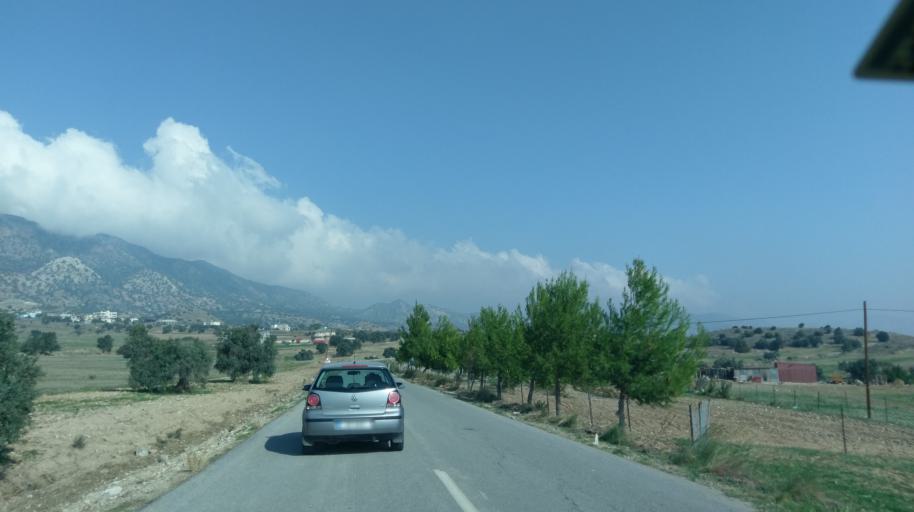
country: CY
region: Ammochostos
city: Lefkonoiko
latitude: 35.2895
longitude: 33.6073
